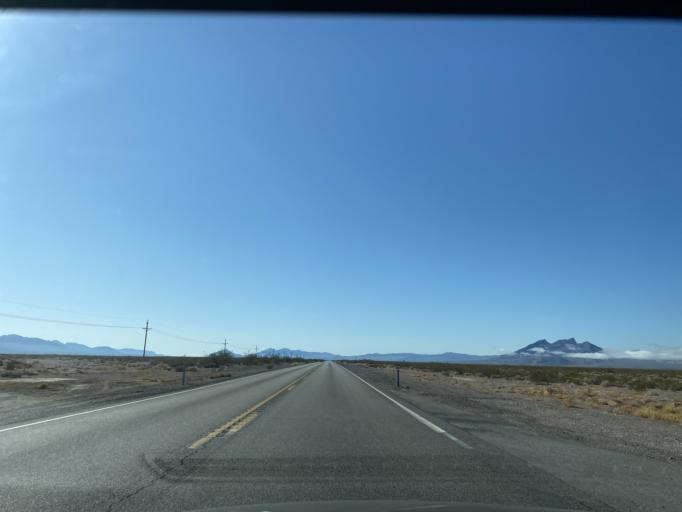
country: US
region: Nevada
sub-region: Nye County
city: Pahrump
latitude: 36.4923
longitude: -116.4215
